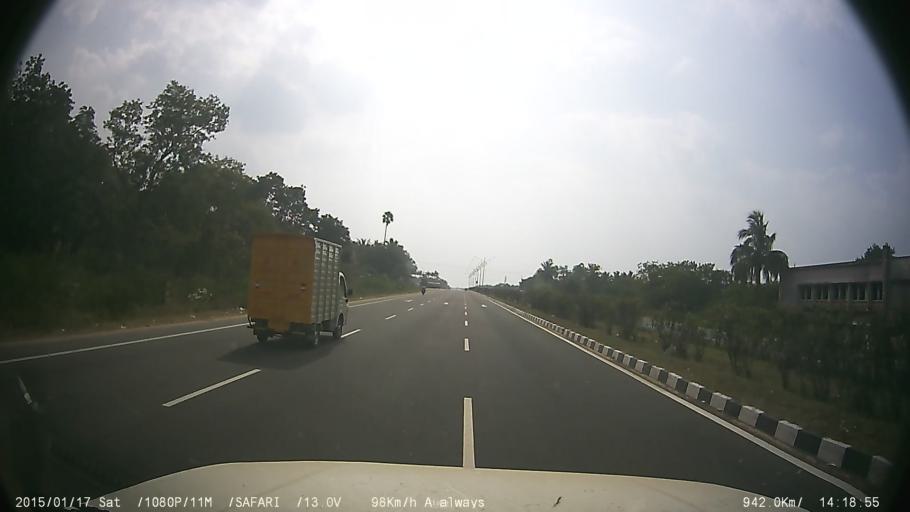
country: IN
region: Tamil Nadu
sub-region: Vellore
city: Vaniyambadi
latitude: 12.7260
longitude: 78.6713
